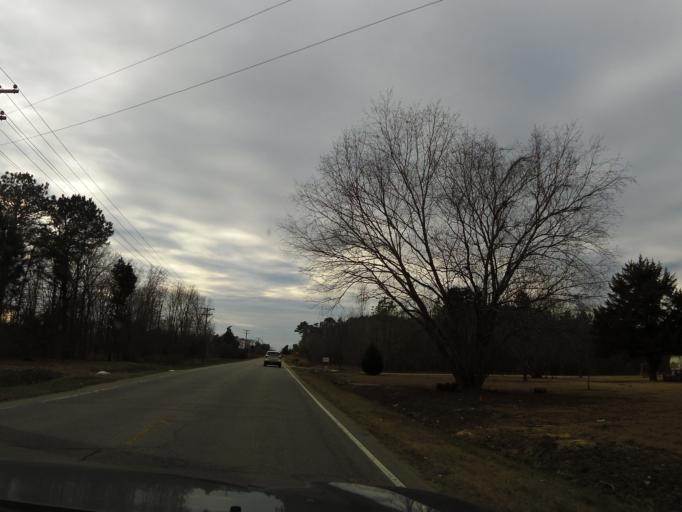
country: US
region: North Carolina
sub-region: Nash County
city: Rocky Mount
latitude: 35.9656
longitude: -77.6792
